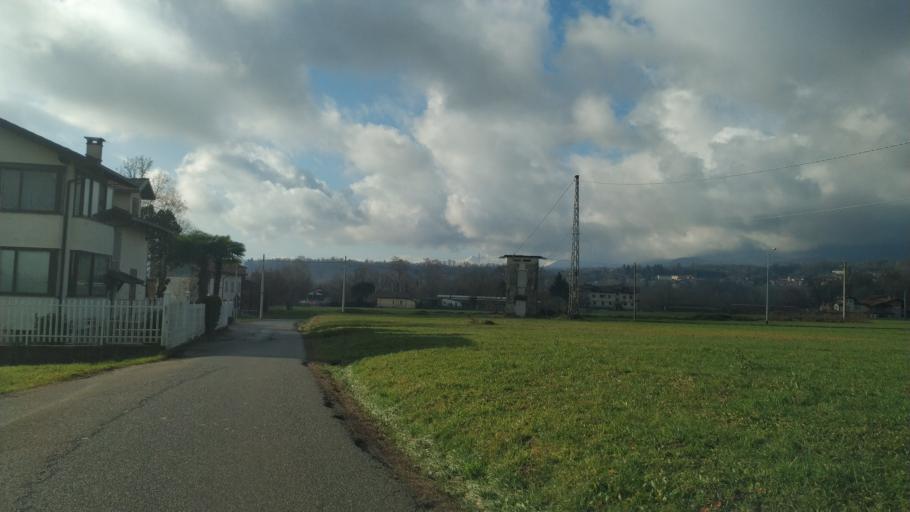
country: IT
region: Piedmont
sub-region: Provincia di Biella
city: Occhieppo Inferiore
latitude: 45.5436
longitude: 8.0263
